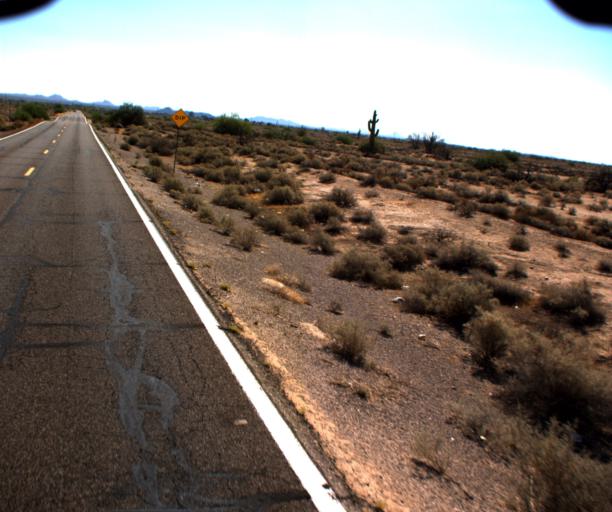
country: US
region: Arizona
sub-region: Pinal County
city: Sacaton
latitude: 33.0569
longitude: -111.6964
